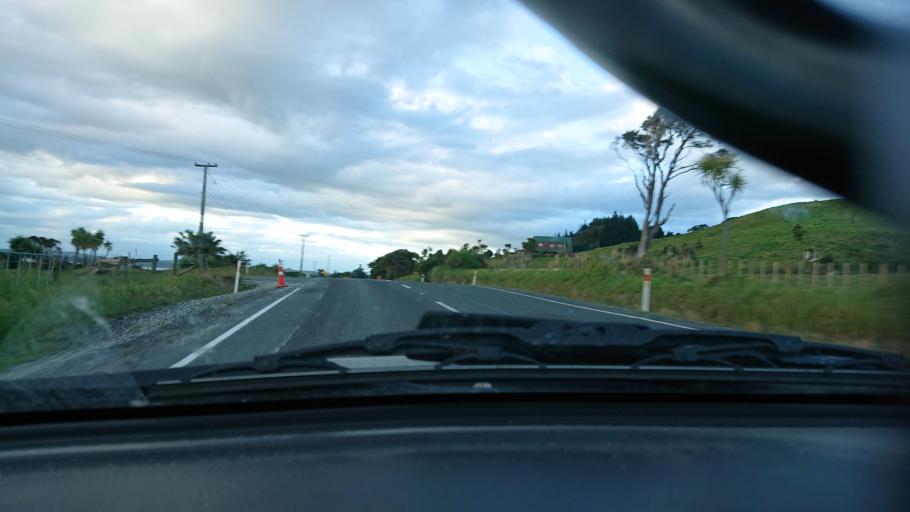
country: NZ
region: Auckland
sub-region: Auckland
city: Wellsford
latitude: -36.4475
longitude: 174.4335
